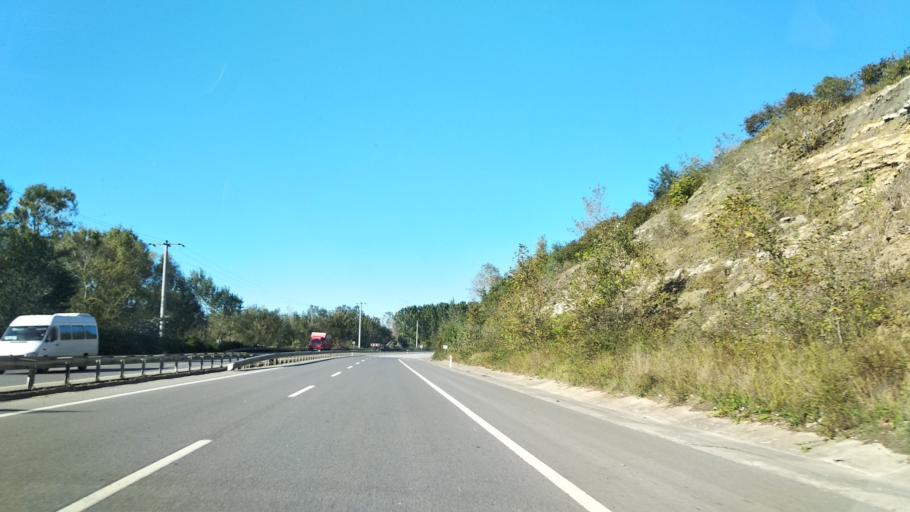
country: TR
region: Sakarya
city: Karasu
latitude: 41.0854
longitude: 30.6477
